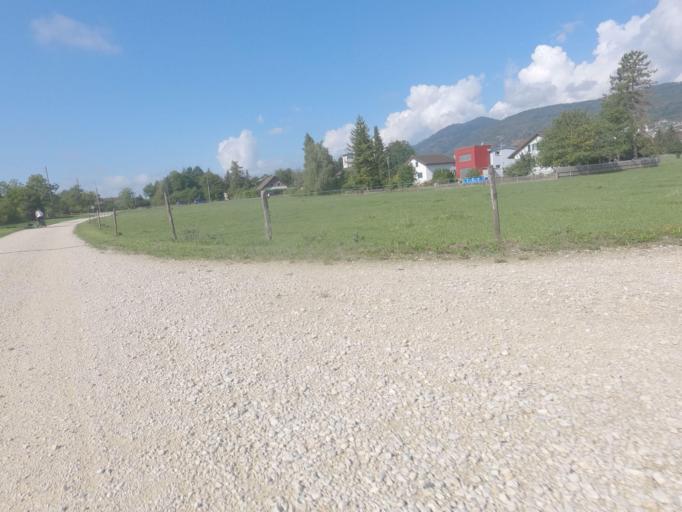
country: CH
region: Solothurn
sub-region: Bezirk Olten
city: Hagendorf
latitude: 47.3294
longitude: 7.8507
